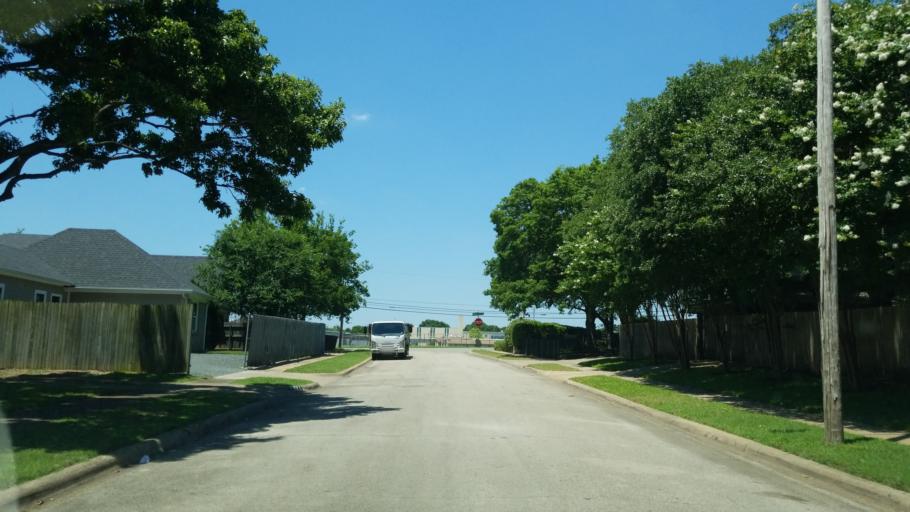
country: US
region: Texas
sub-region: Dallas County
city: University Park
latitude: 32.8797
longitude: -96.8484
